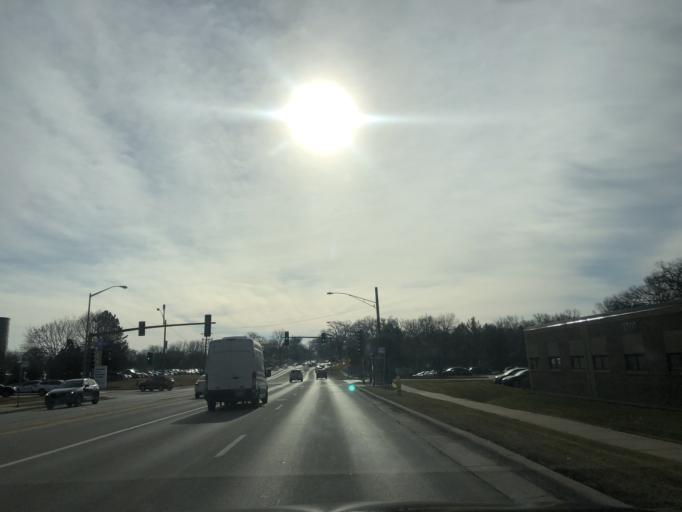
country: US
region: Illinois
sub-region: DuPage County
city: Downers Grove
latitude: 41.8190
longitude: -88.0104
